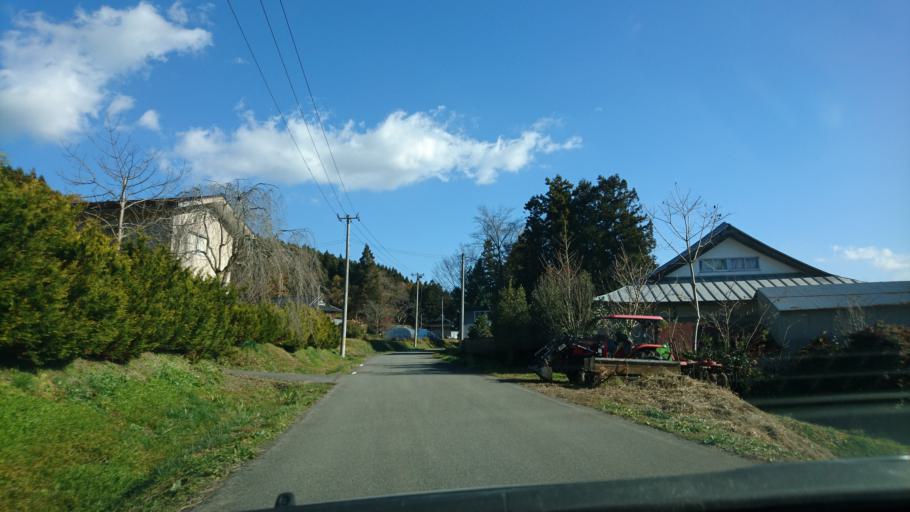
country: JP
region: Iwate
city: Ichinoseki
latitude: 39.0011
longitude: 141.0828
